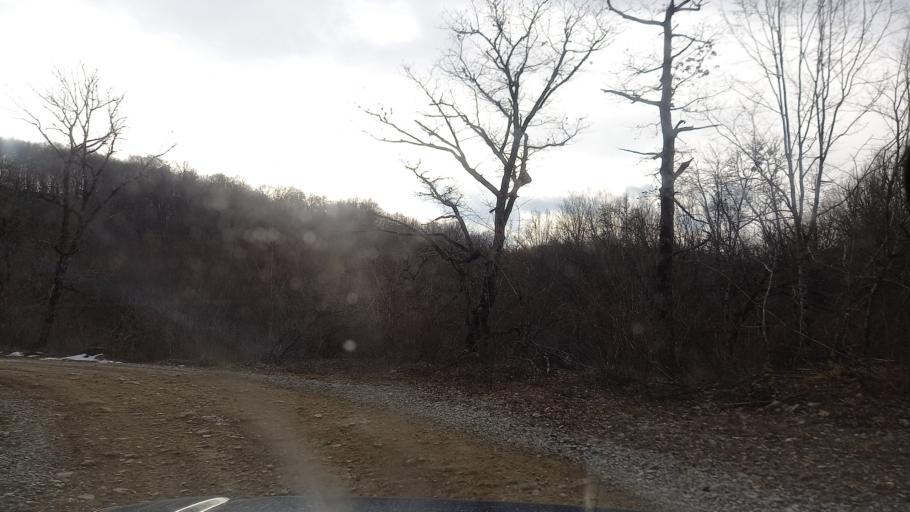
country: RU
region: Adygeya
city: Kamennomostskiy
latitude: 44.1515
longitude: 40.2957
